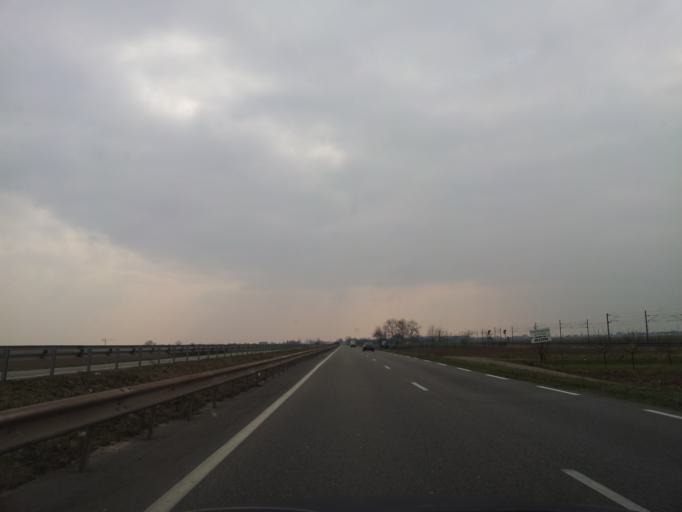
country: FR
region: Alsace
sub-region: Departement du Bas-Rhin
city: Erstein
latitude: 48.4403
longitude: 7.6501
